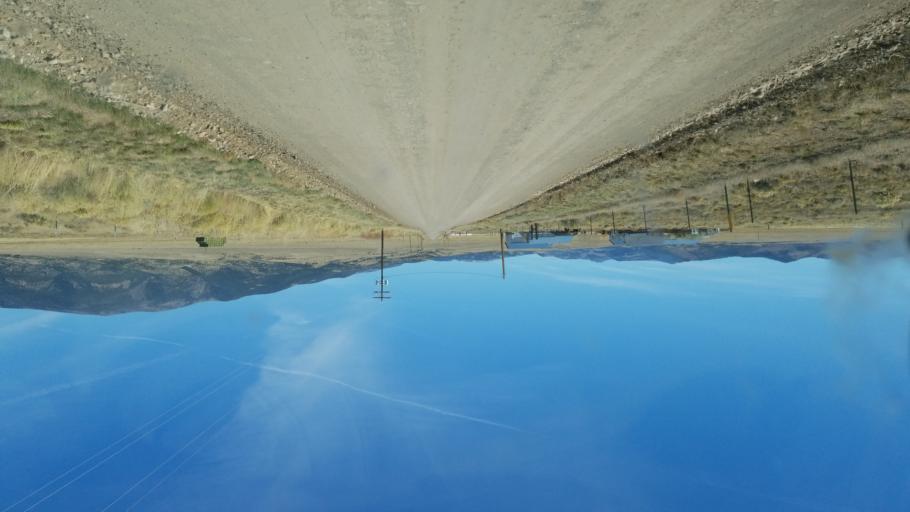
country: US
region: Colorado
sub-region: Rio Grande County
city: Monte Vista
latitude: 37.4011
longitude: -106.1435
